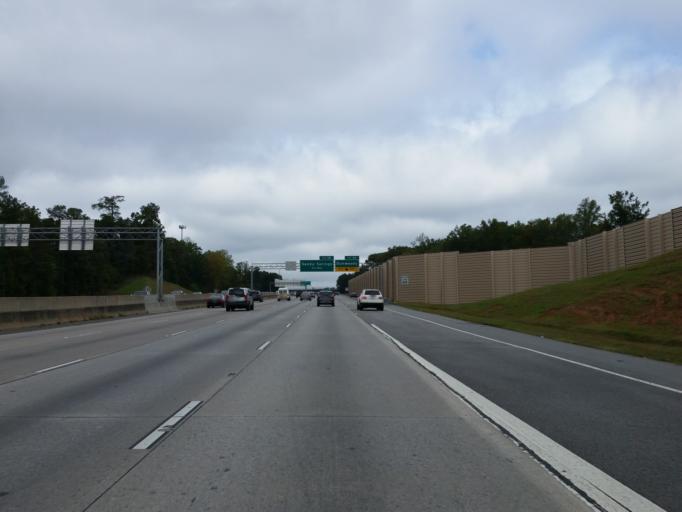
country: US
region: Georgia
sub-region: Fulton County
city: Sandy Springs
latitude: 33.9228
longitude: -84.3577
